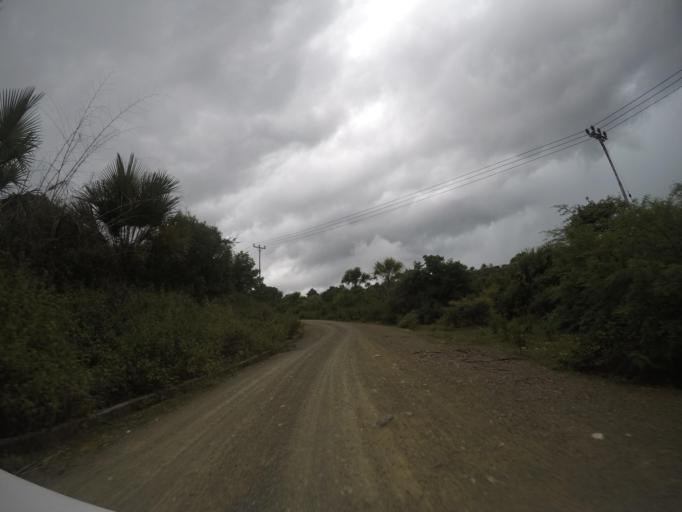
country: TL
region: Bobonaro
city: Maliana
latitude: -8.8511
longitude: 125.0697
